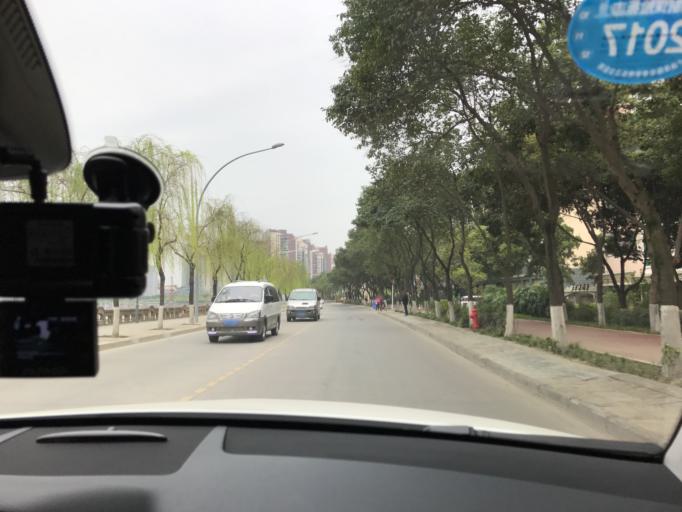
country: CN
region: Sichuan
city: Mianyang
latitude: 31.4593
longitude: 104.7014
